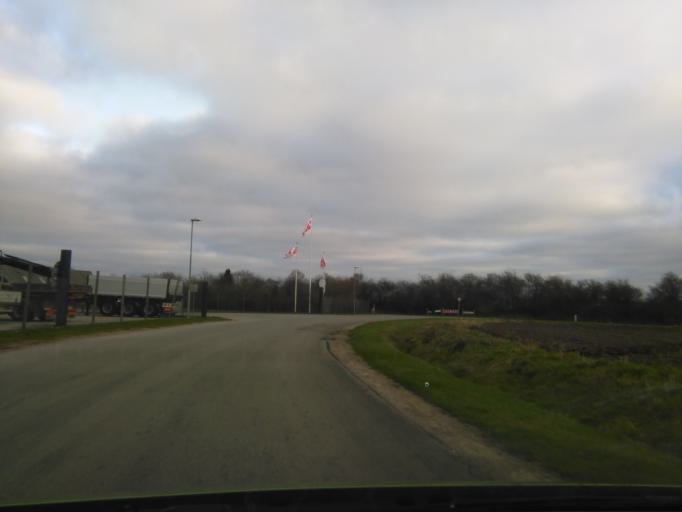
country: DK
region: Central Jutland
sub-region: Arhus Kommune
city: Stavtrup
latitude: 56.1779
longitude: 10.0953
